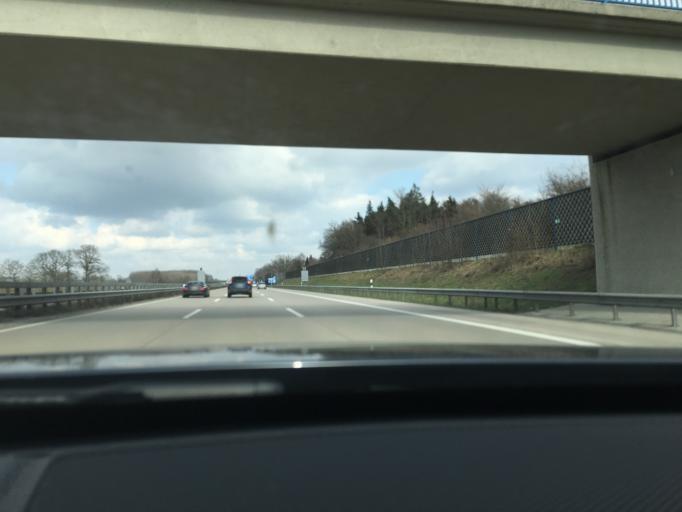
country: DE
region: Lower Saxony
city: Buehren
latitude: 52.8056
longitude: 8.2086
